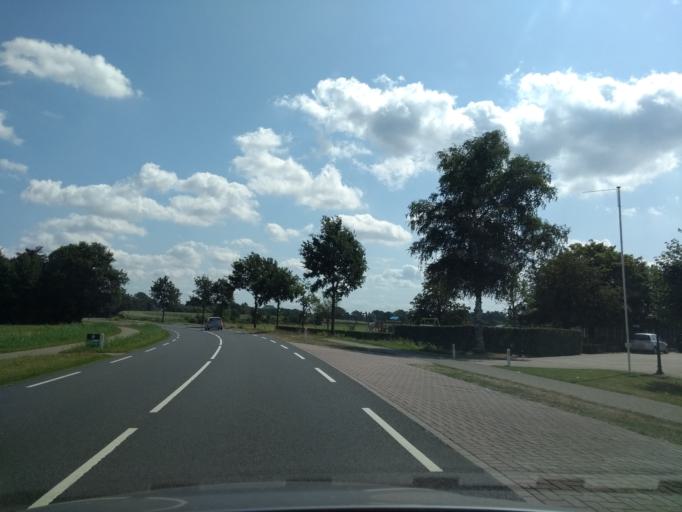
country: DE
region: Lower Saxony
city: Lage
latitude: 52.4061
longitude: 6.9257
